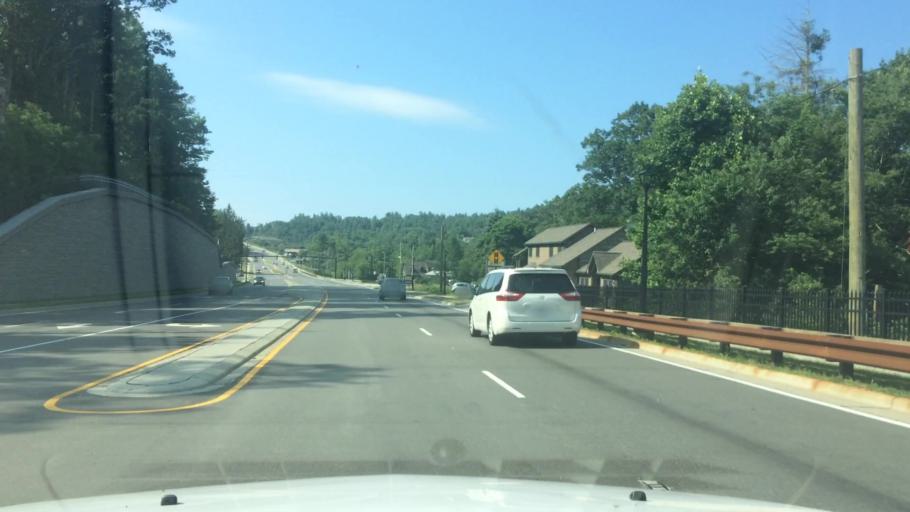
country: US
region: North Carolina
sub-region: Watauga County
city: Blowing Rock
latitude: 36.1350
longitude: -81.6712
